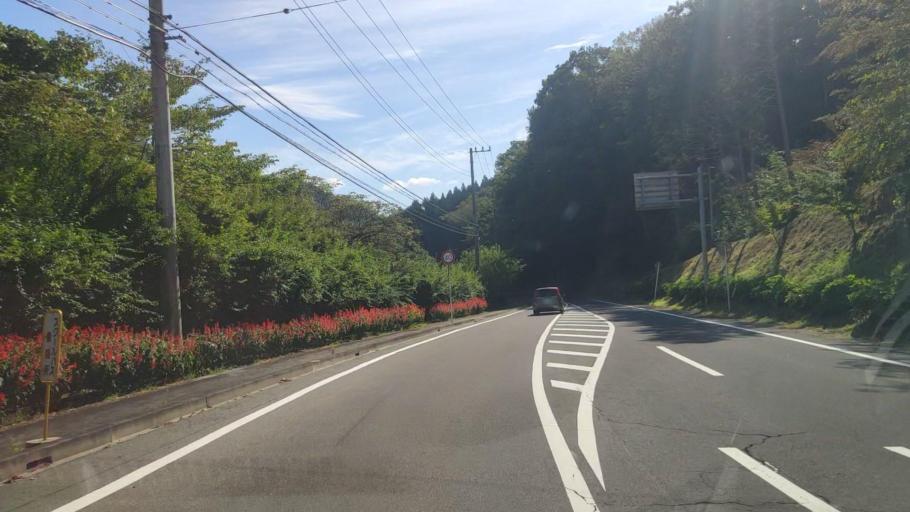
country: JP
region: Gunma
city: Nakanojomachi
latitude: 36.6225
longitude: 138.7698
